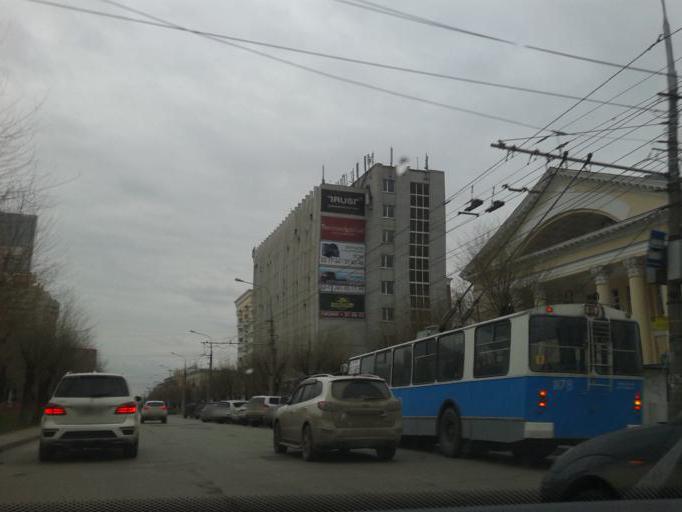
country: RU
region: Volgograd
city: Volgograd
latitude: 48.7188
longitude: 44.5067
